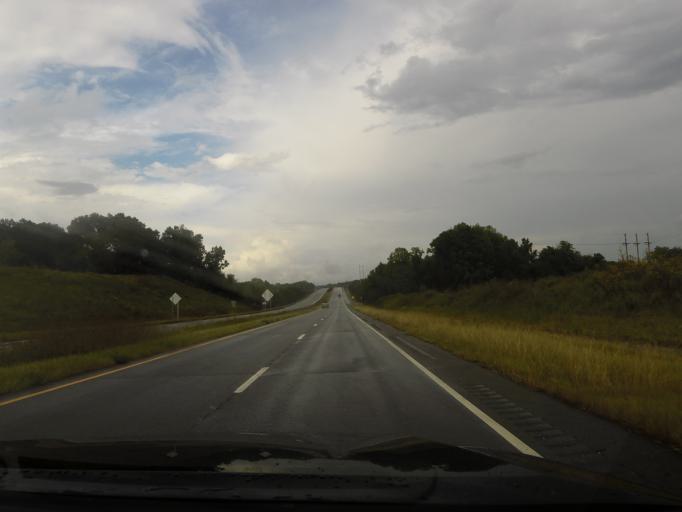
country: US
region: Georgia
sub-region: Wayne County
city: Jesup
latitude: 31.6638
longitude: -81.8447
